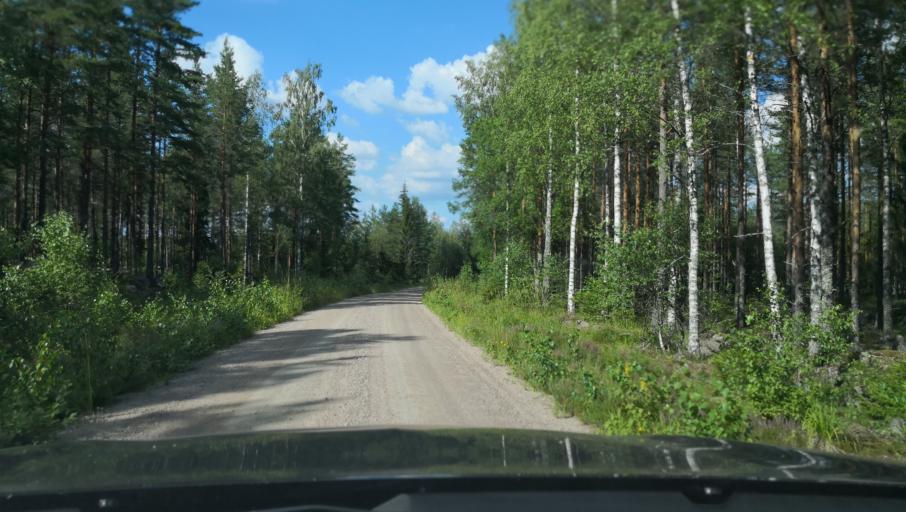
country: SE
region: Vaestmanland
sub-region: Vasteras
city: Skultuna
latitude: 59.7147
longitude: 16.3708
